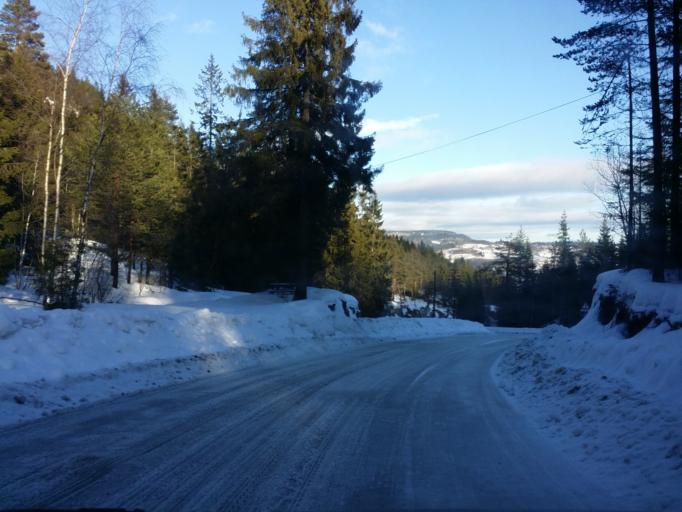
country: NO
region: Buskerud
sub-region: Lier
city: Lierbyen
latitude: 59.8226
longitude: 10.1852
